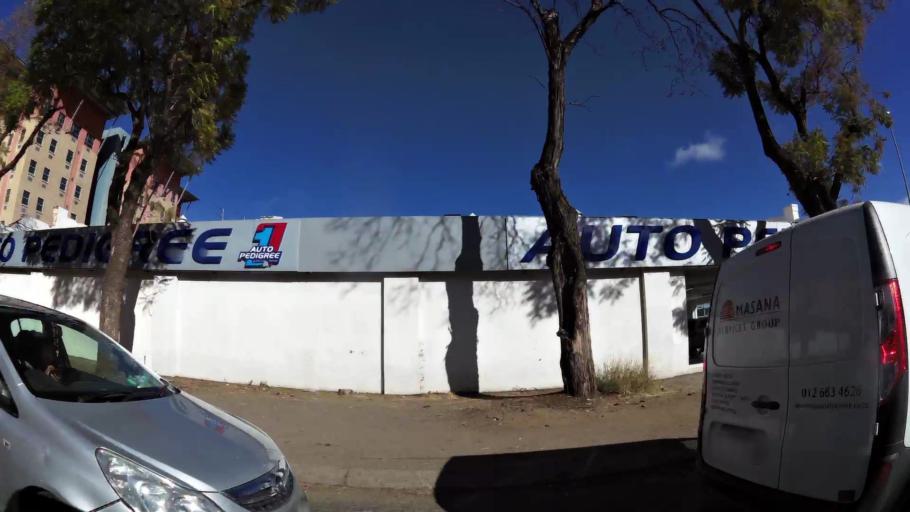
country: ZA
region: Limpopo
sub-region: Capricorn District Municipality
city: Polokwane
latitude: -23.9122
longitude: 29.4503
